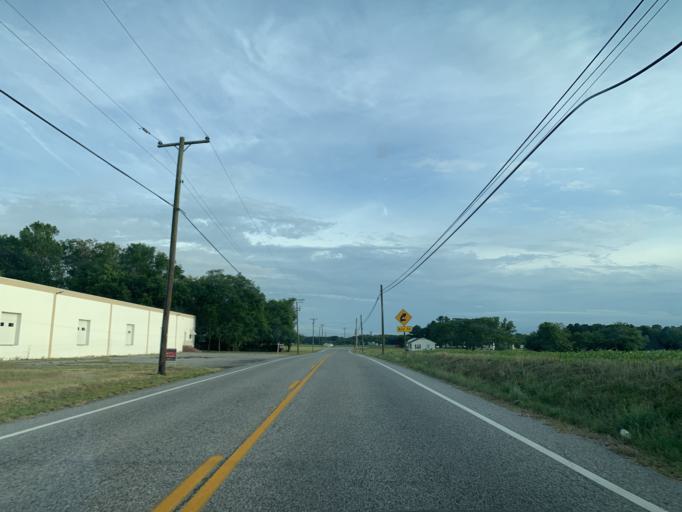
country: US
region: Maryland
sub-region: Worcester County
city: Snow Hill
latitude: 38.1582
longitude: -75.4036
